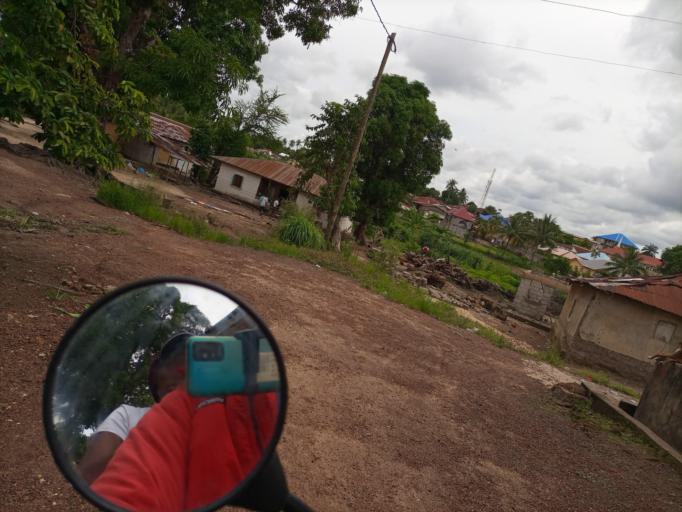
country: SL
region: Southern Province
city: Bo
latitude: 7.9544
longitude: -11.7456
